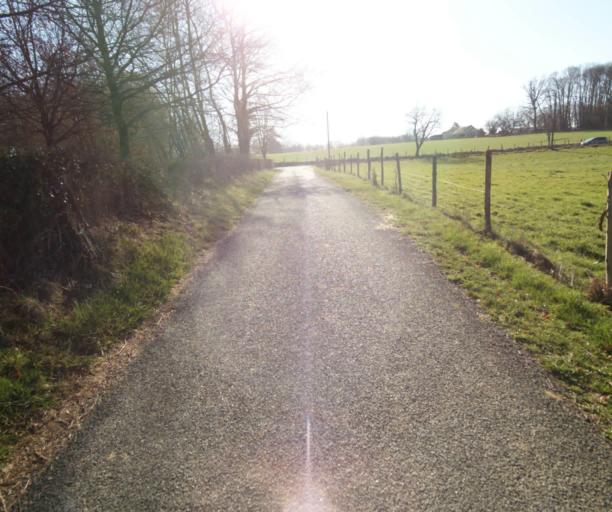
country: FR
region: Limousin
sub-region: Departement de la Correze
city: Saint-Clement
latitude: 45.3738
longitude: 1.6631
